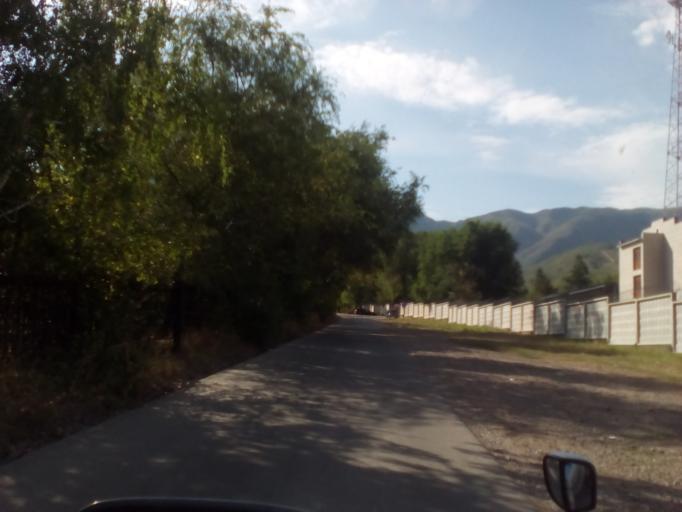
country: KZ
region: Almaty Oblysy
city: Burunday
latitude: 43.1608
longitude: 76.3820
